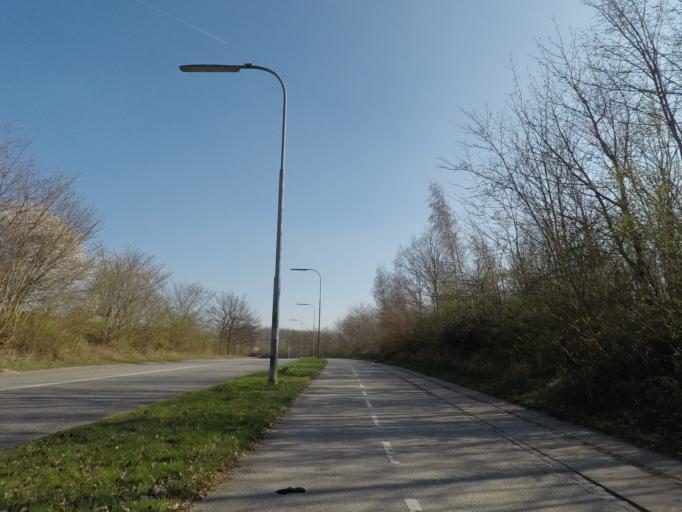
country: DK
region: Capital Region
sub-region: Ballerup Kommune
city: Ballerup
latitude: 55.7466
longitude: 12.3839
